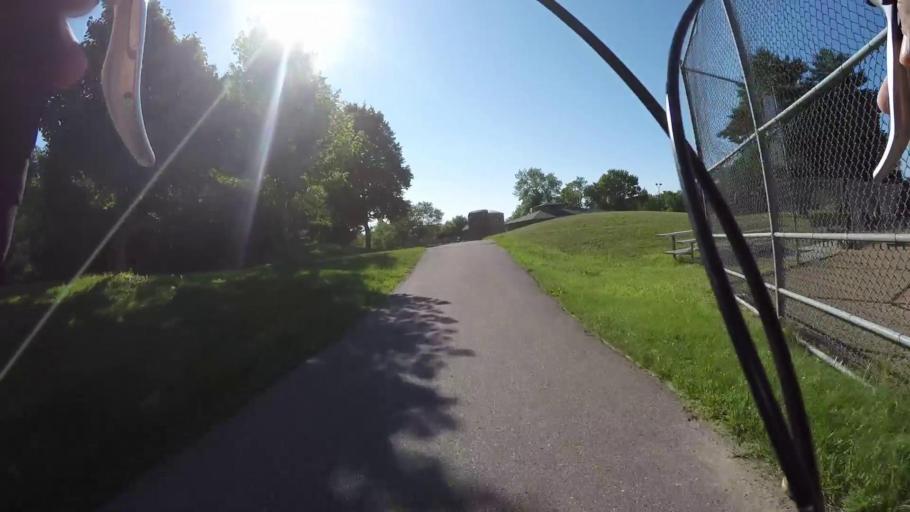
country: US
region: Minnesota
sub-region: Carver County
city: Chanhassen
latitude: 44.8775
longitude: -93.5008
